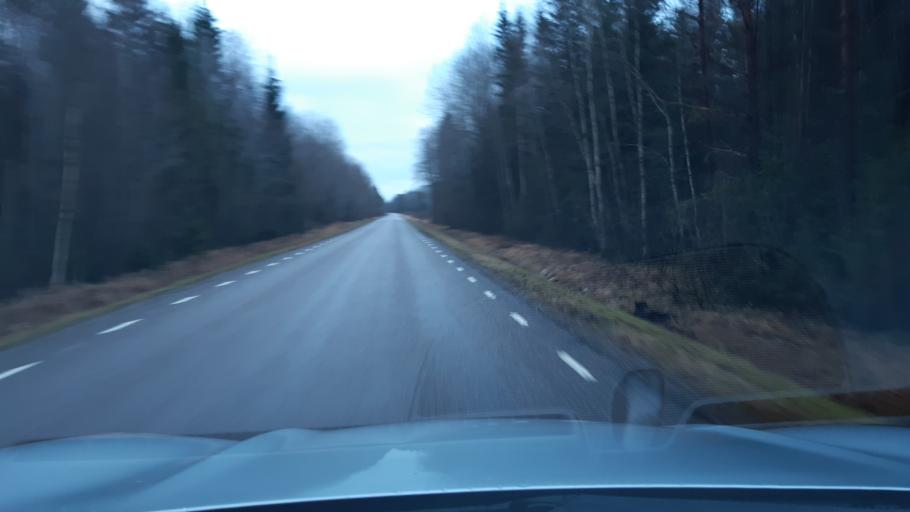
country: EE
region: Raplamaa
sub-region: Kohila vald
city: Kohila
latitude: 59.1370
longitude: 24.6589
